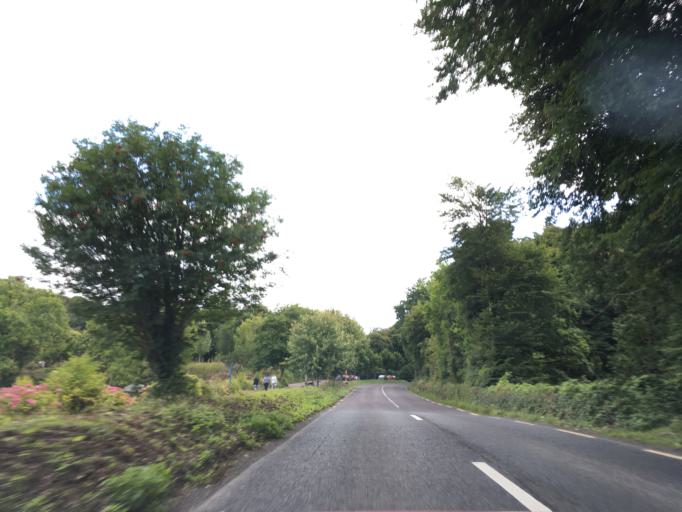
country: IE
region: Munster
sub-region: County Cork
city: Crosshaven
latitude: 51.8039
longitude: -8.3358
